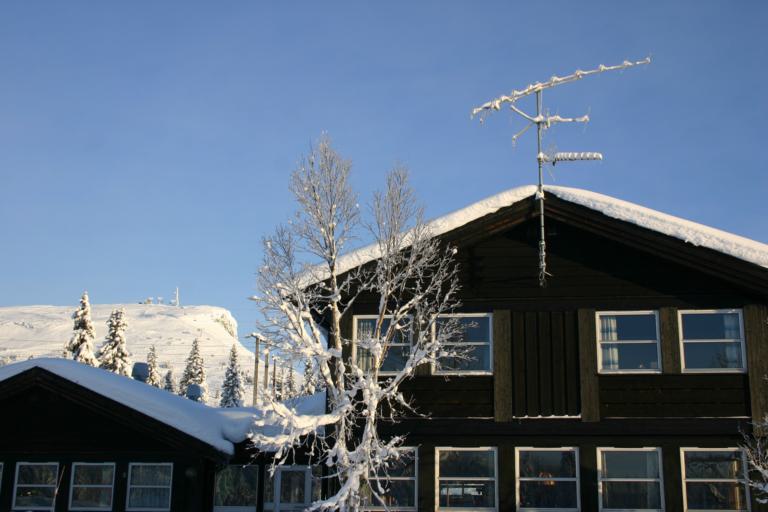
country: NO
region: Oppland
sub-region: Gausdal
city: Segalstad bru
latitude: 61.3353
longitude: 10.0798
